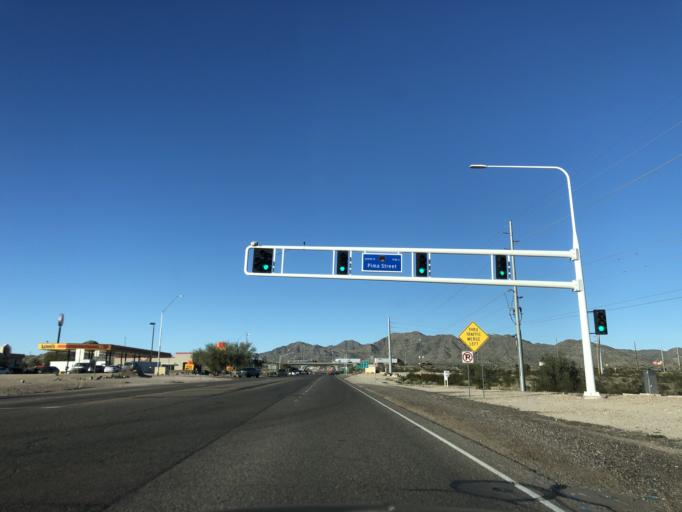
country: US
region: Arizona
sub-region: Maricopa County
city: Buckeye
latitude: 33.4301
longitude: -112.5909
